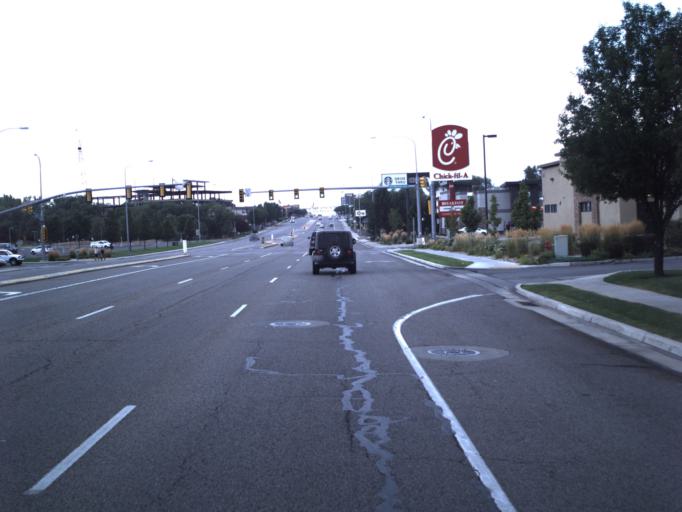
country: US
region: Utah
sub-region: Salt Lake County
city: Murray
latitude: 40.6585
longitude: -111.8882
